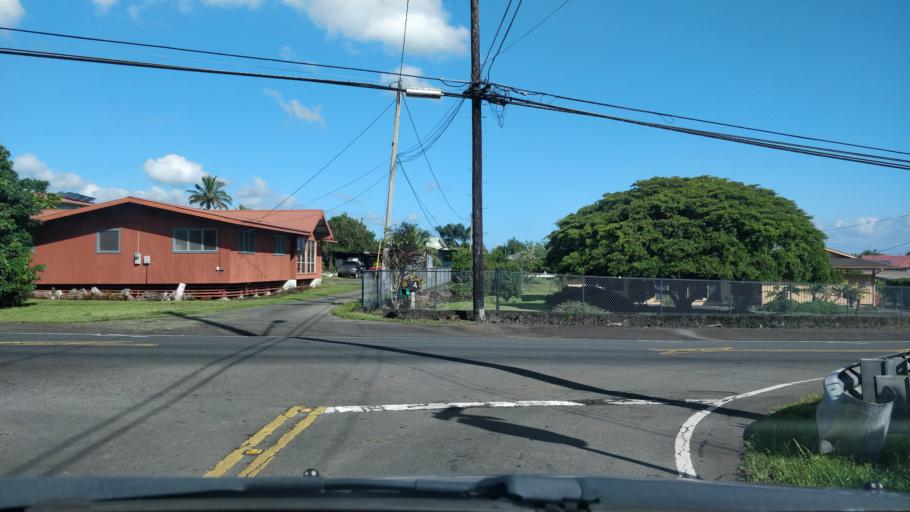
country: US
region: Hawaii
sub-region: Hawaii County
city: Hilo
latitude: 19.6649
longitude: -155.0995
